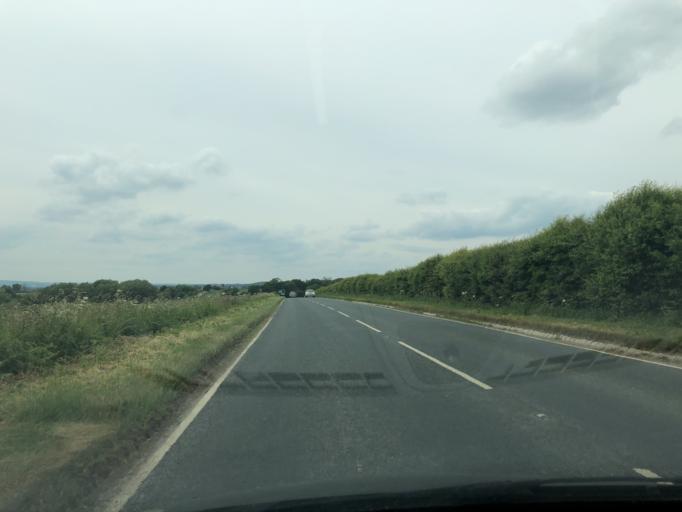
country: GB
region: England
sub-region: North Yorkshire
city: Great Habton
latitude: 54.2634
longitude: -0.8857
